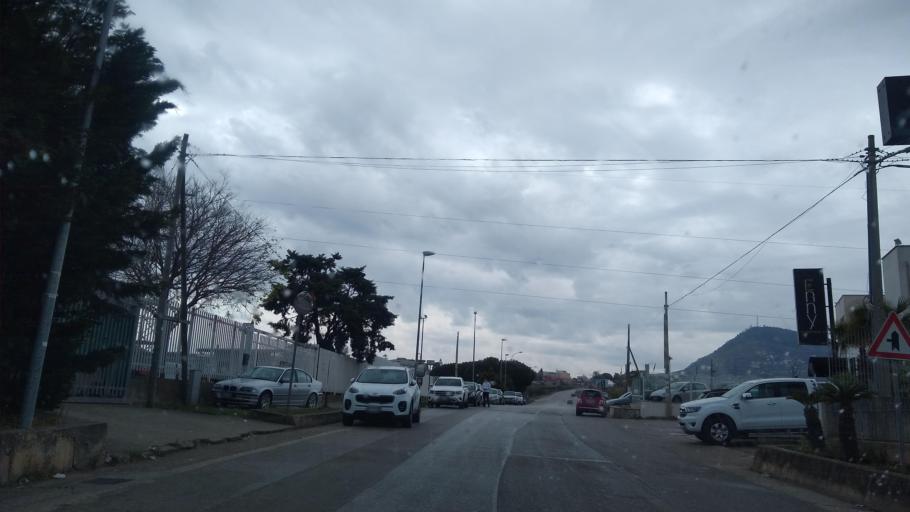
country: IT
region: Sicily
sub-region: Trapani
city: Alcamo
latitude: 38.0014
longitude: 12.9561
